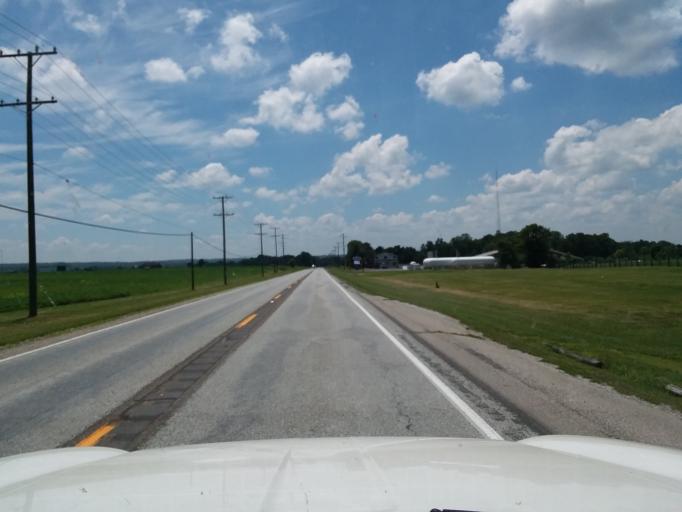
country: US
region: Indiana
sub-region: Johnson County
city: Trafalgar
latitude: 39.3800
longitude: -86.2445
